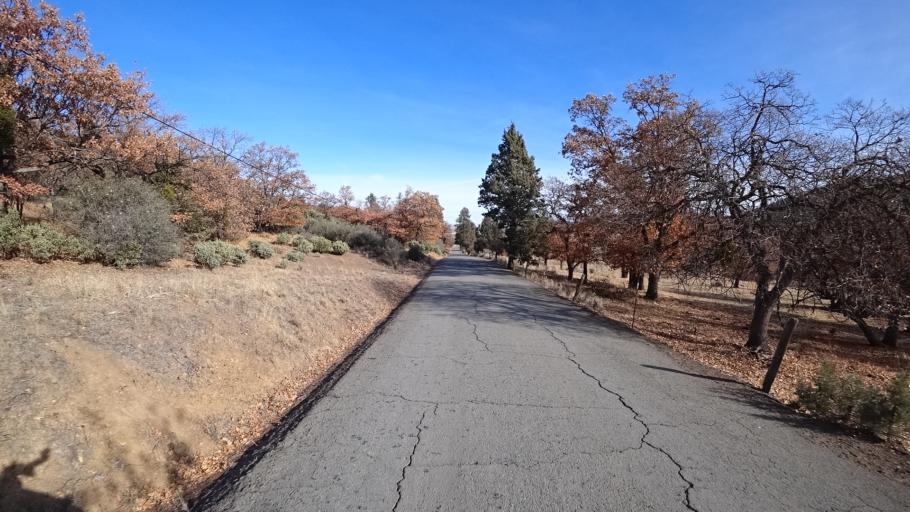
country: US
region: California
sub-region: Siskiyou County
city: Montague
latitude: 41.6222
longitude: -122.5758
